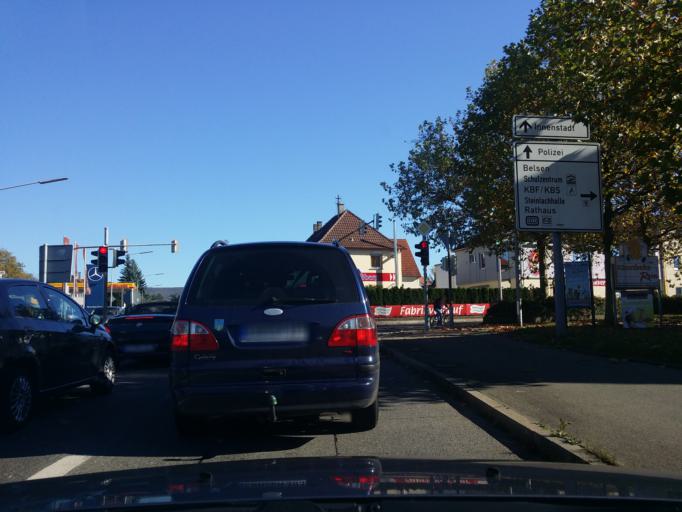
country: DE
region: Baden-Wuerttemberg
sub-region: Tuebingen Region
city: Mossingen
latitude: 48.4066
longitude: 9.0483
